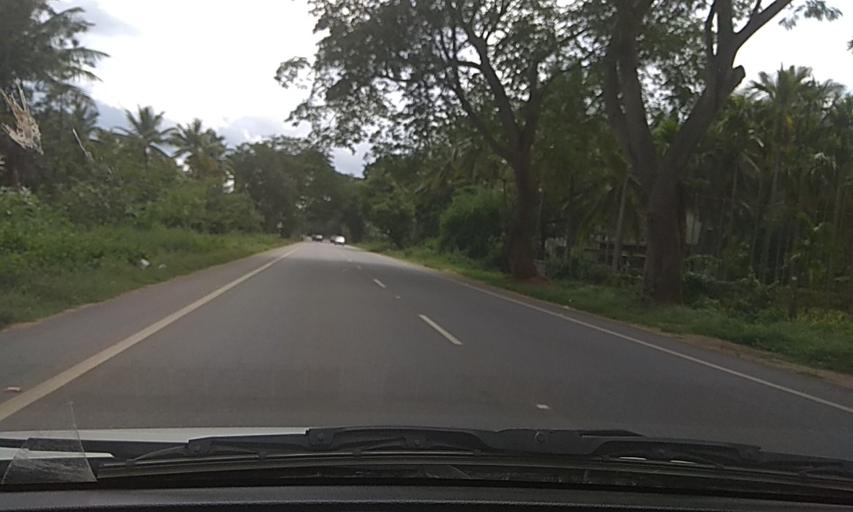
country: IN
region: Karnataka
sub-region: Tumkur
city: Tumkur
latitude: 13.2445
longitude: 77.0796
